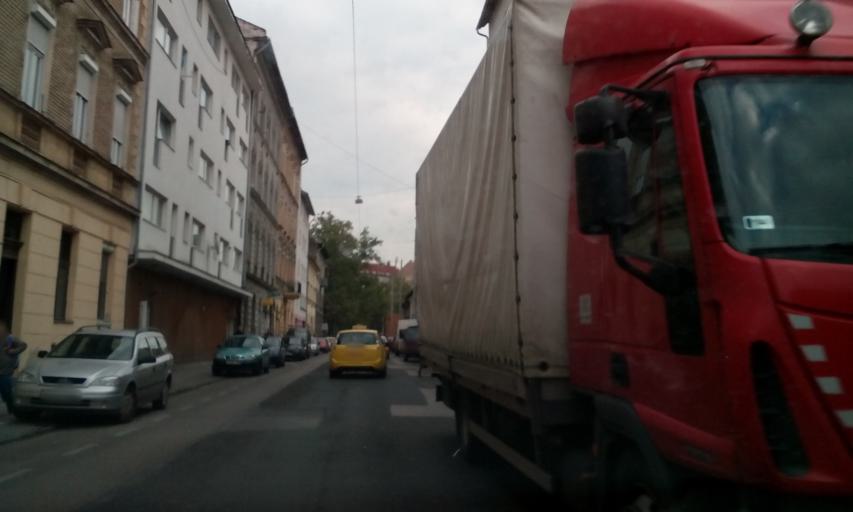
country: HU
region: Budapest
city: Budapest VIII. keruelet
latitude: 47.4900
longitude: 19.0835
